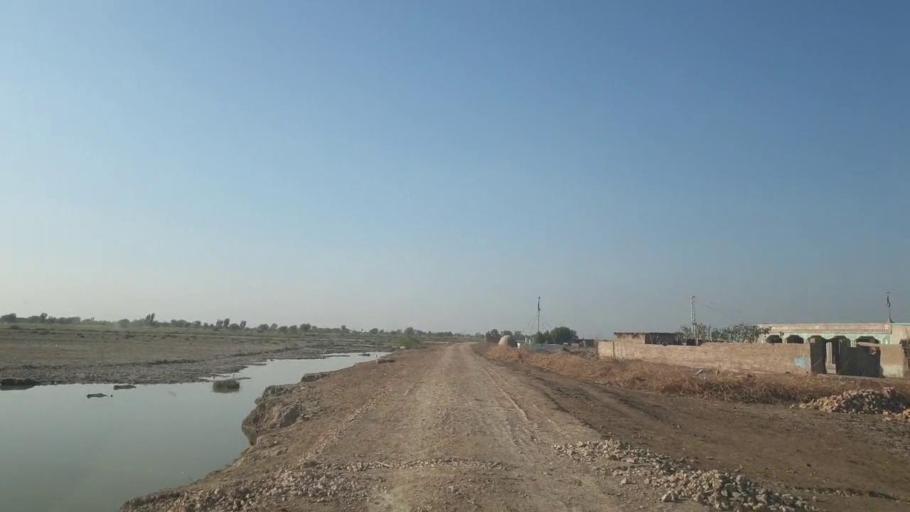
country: PK
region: Sindh
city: Mirwah Gorchani
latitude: 25.4239
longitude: 69.1304
